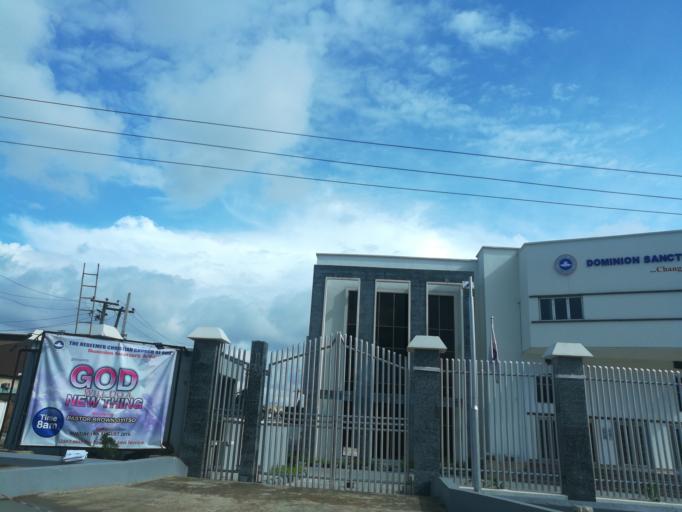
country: NG
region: Lagos
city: Agege
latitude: 6.6268
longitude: 3.3479
